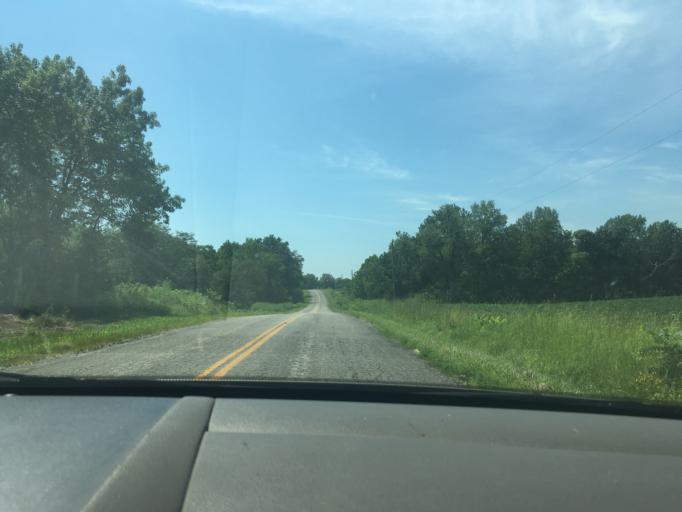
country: US
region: Missouri
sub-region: Gentry County
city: Stanberry
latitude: 40.2200
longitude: -94.7254
